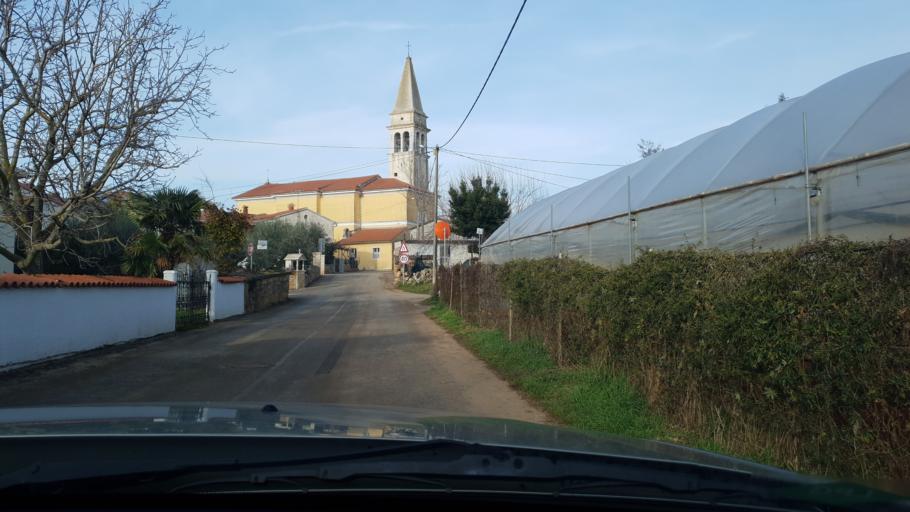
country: HR
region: Istarska
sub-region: Grad Porec
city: Porec
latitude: 45.2623
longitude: 13.6599
